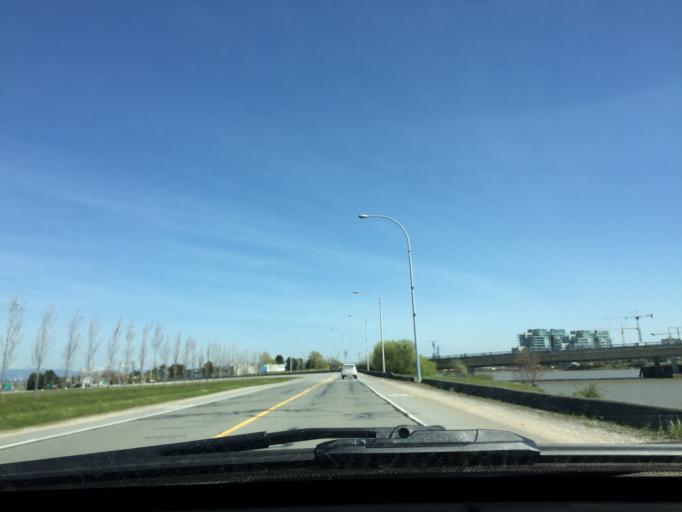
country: CA
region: British Columbia
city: Richmond
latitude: 49.1779
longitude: -123.1593
